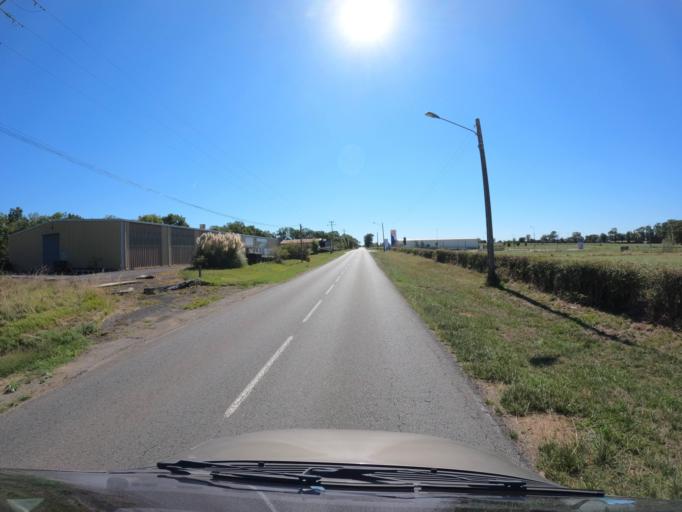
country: FR
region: Poitou-Charentes
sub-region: Departement de la Vienne
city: Lathus-Saint-Remy
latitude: 46.3430
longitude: 0.9524
